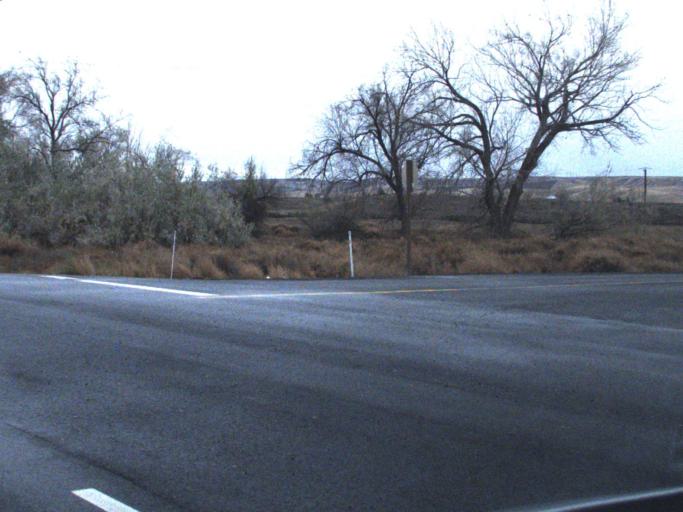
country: US
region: Washington
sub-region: Walla Walla County
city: Garrett
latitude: 46.0424
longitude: -118.6890
